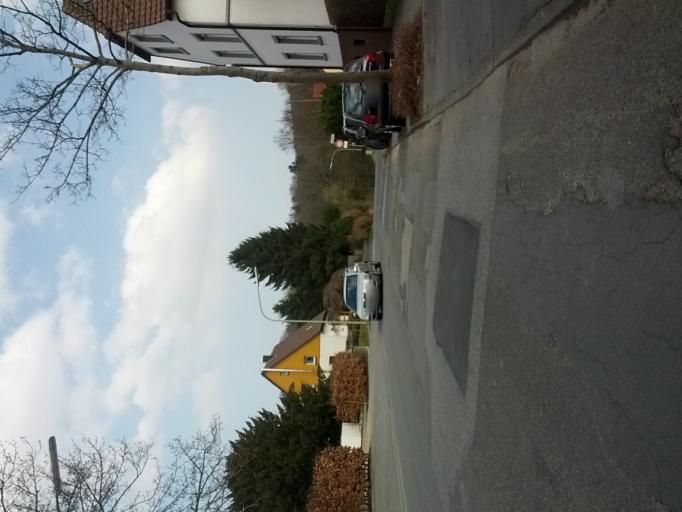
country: DE
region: North Rhine-Westphalia
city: Wickede
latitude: 51.4525
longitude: 7.9781
